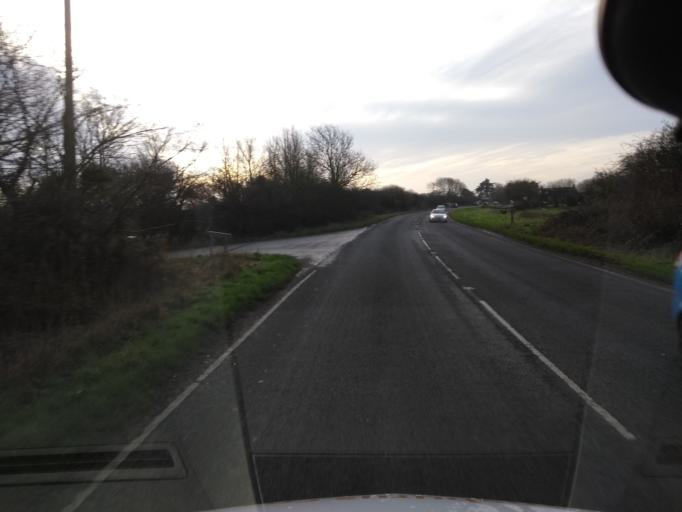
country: GB
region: England
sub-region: North Somerset
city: Bleadon
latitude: 51.2794
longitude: -2.9337
